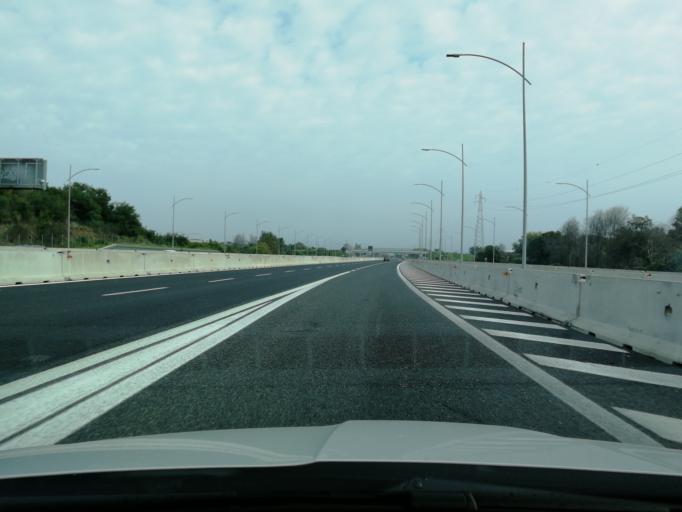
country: IT
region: Latium
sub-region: Citta metropolitana di Roma Capitale
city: Setteville
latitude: 41.9237
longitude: 12.6228
